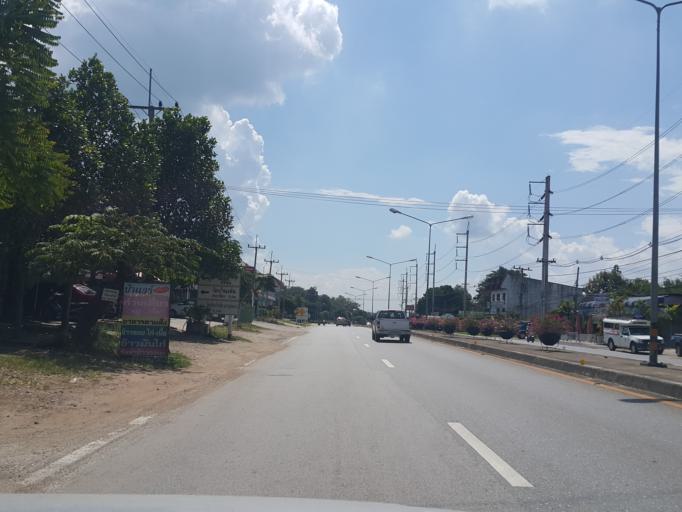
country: TH
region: Chiang Mai
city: Mae Taeng
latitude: 19.1343
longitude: 98.9489
